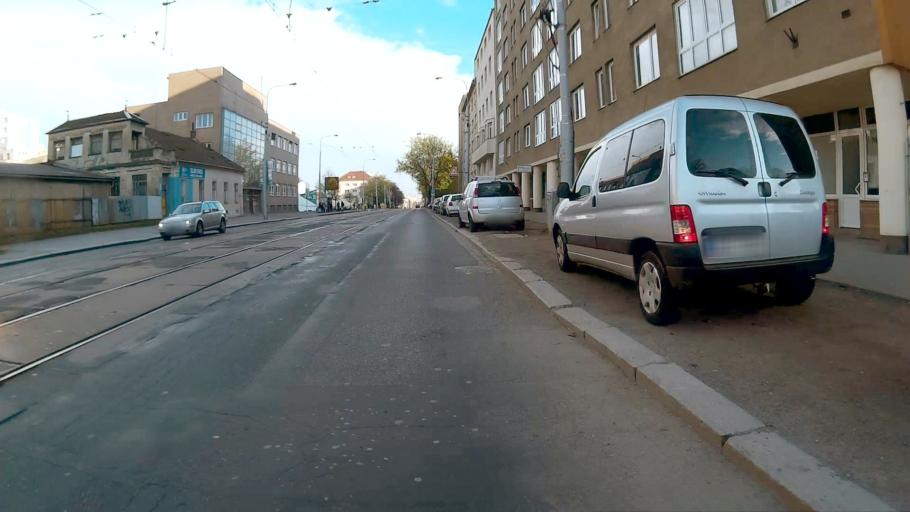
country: CZ
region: South Moravian
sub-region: Mesto Brno
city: Mokra Hora
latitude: 49.2312
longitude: 16.5902
